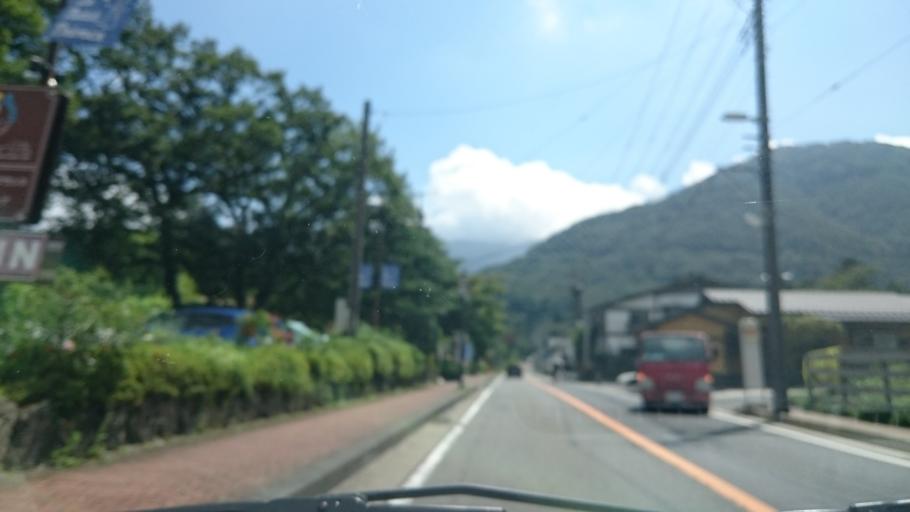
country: JP
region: Shizuoka
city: Gotemba
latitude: 35.2674
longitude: 139.0127
